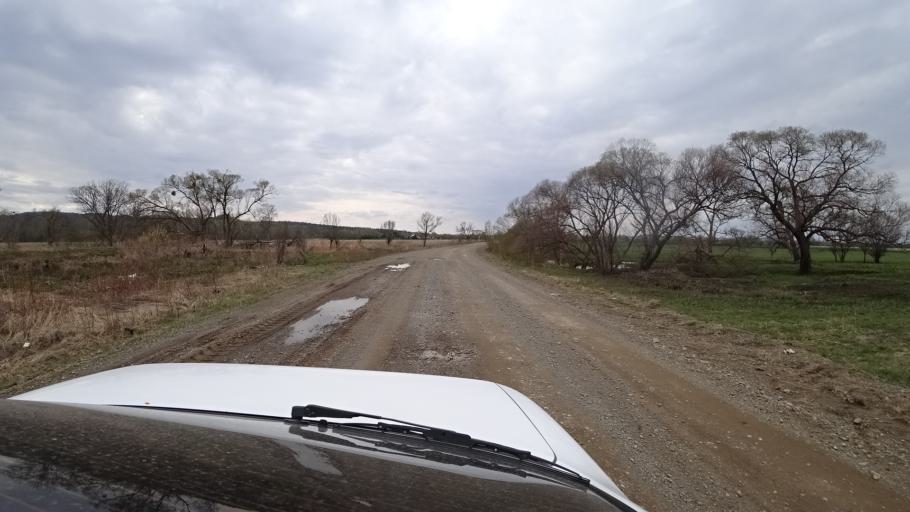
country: RU
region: Primorskiy
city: Novopokrovka
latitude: 45.4900
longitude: 134.4584
